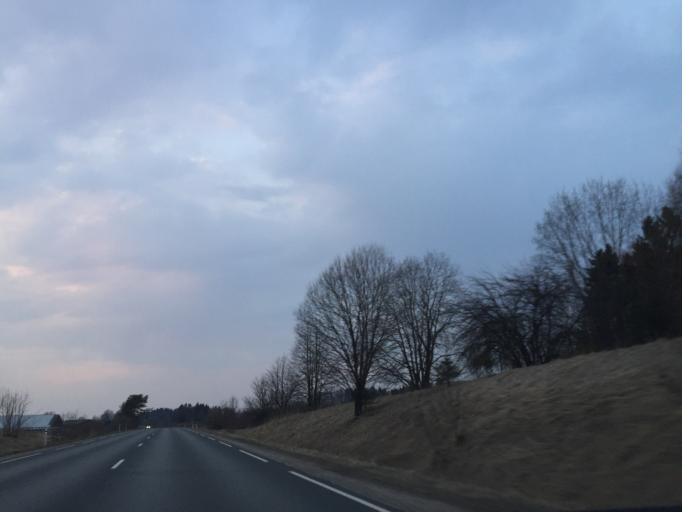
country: LV
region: Raunas
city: Rauna
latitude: 57.2508
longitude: 25.5482
